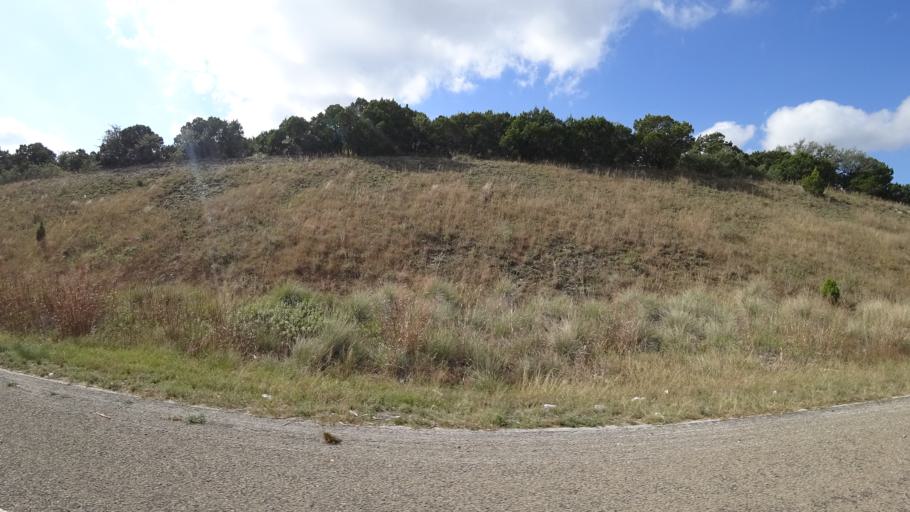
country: US
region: Texas
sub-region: Travis County
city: Barton Creek
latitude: 30.2699
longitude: -97.8957
